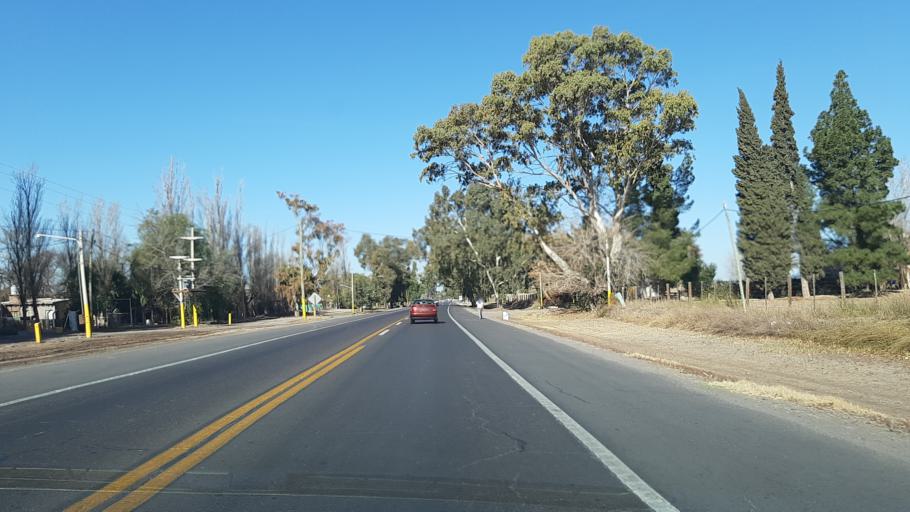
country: AR
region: San Juan
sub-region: Departamento de Santa Lucia
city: Santa Lucia
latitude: -31.5646
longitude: -68.4511
